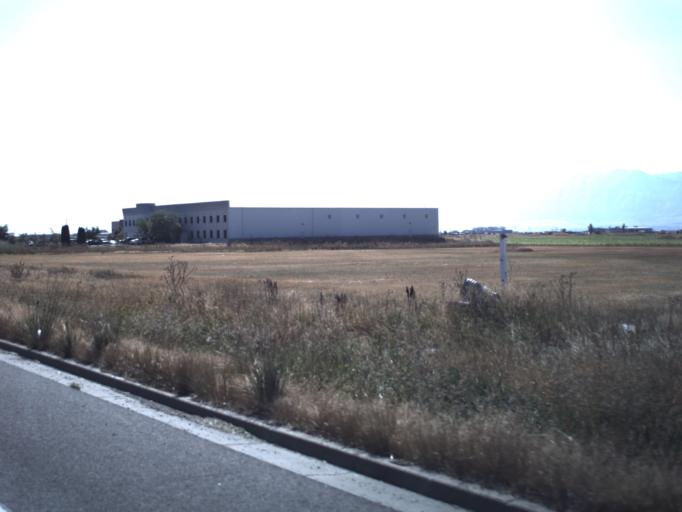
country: US
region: Utah
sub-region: Cache County
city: Hyde Park
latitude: 41.7860
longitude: -111.8339
